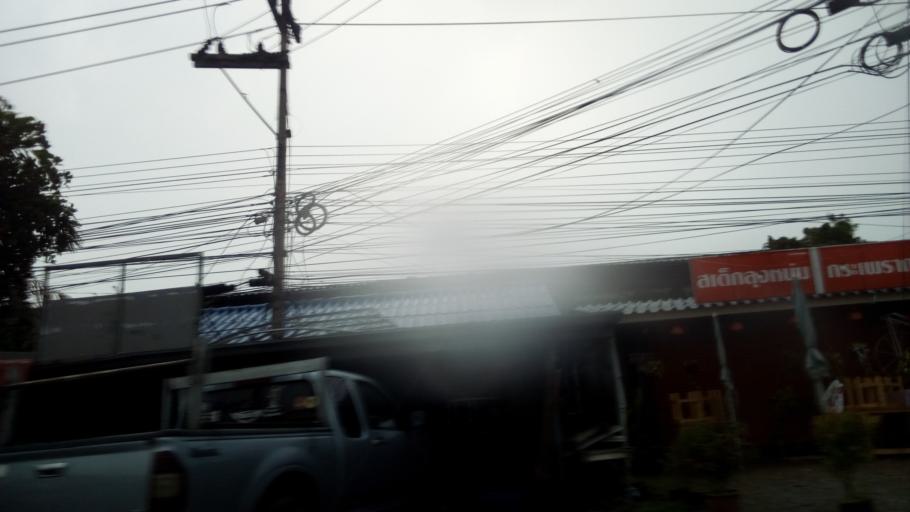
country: TH
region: Phra Nakhon Si Ayutthaya
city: Phra Nakhon Si Ayutthaya
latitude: 14.3443
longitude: 100.5847
